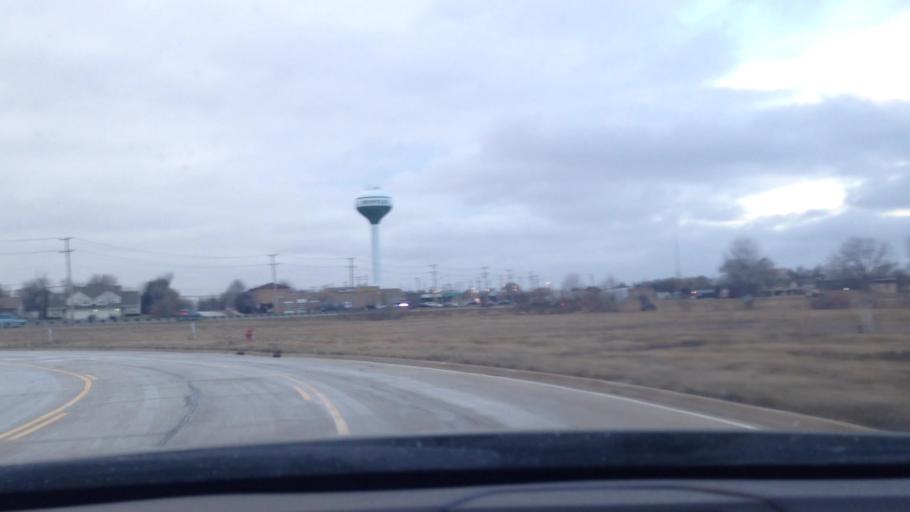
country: US
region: Illinois
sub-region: McHenry County
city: Huntley
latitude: 42.1818
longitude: -88.4249
